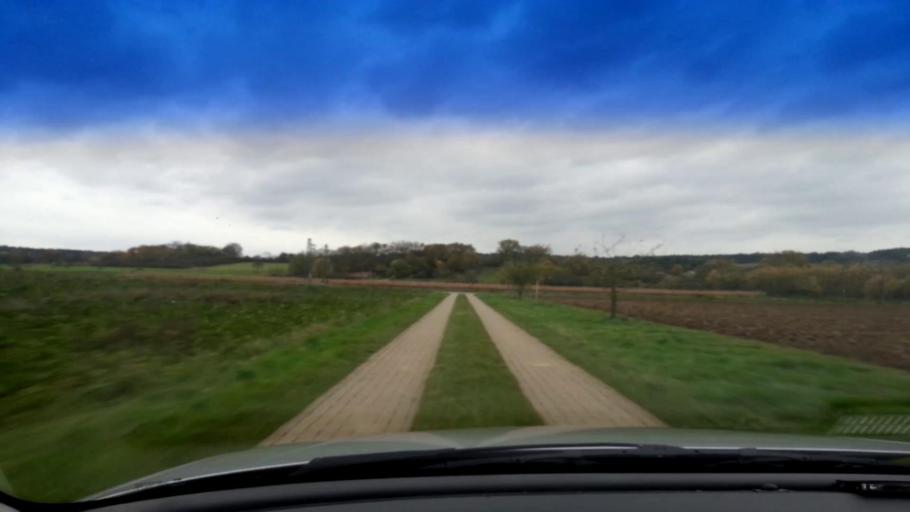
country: DE
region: Bavaria
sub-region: Upper Franconia
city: Oberhaid
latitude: 49.9283
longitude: 10.8315
